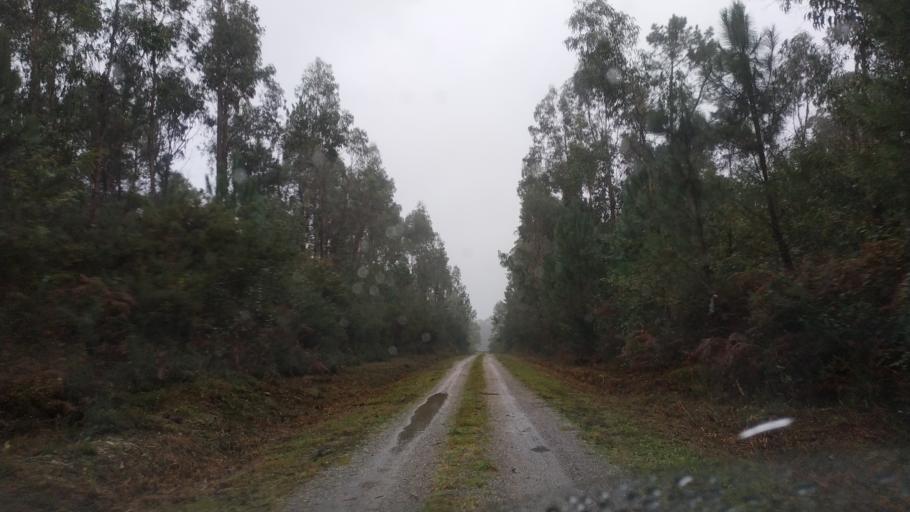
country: ES
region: Galicia
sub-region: Provincia da Coruna
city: Negreira
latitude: 42.9075
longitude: -8.7641
